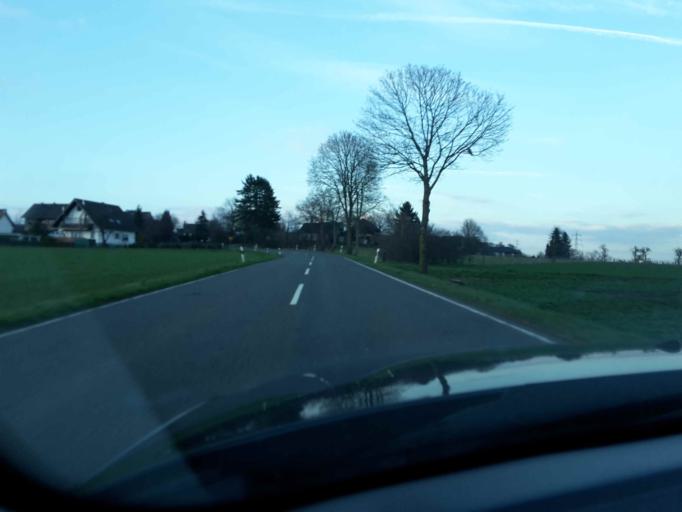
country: DE
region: North Rhine-Westphalia
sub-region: Regierungsbezirk Koln
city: Hennef
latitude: 50.7102
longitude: 7.3135
